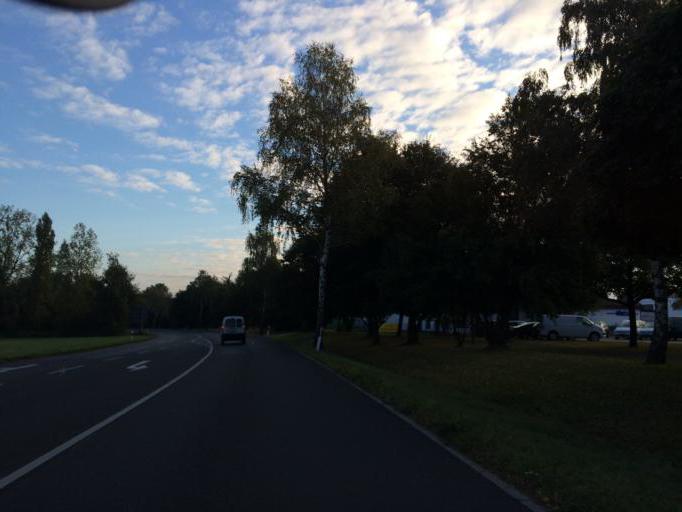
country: DE
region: North Rhine-Westphalia
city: Sankt Augustin
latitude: 50.7579
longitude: 7.1709
